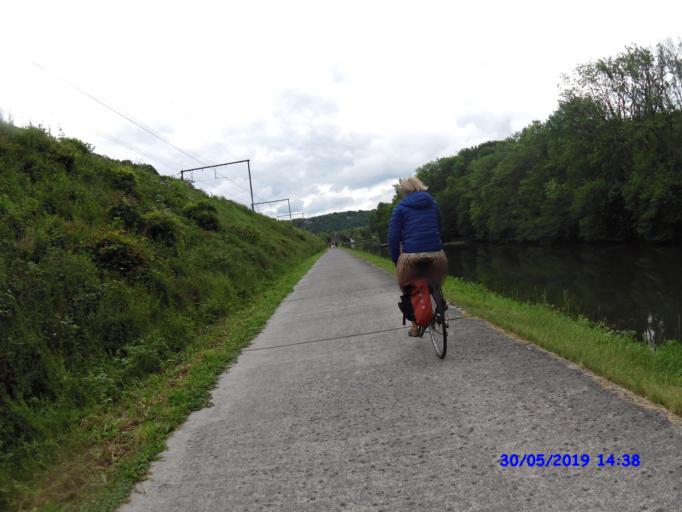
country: BE
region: Wallonia
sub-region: Province du Hainaut
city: Thuin
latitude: 50.3745
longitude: 4.3410
